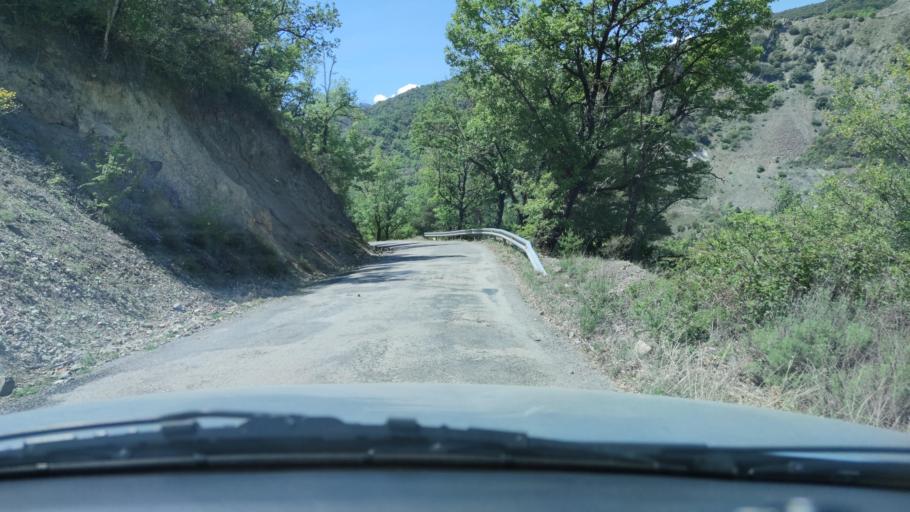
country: ES
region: Catalonia
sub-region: Provincia de Lleida
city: Sort
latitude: 42.3166
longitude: 1.0650
